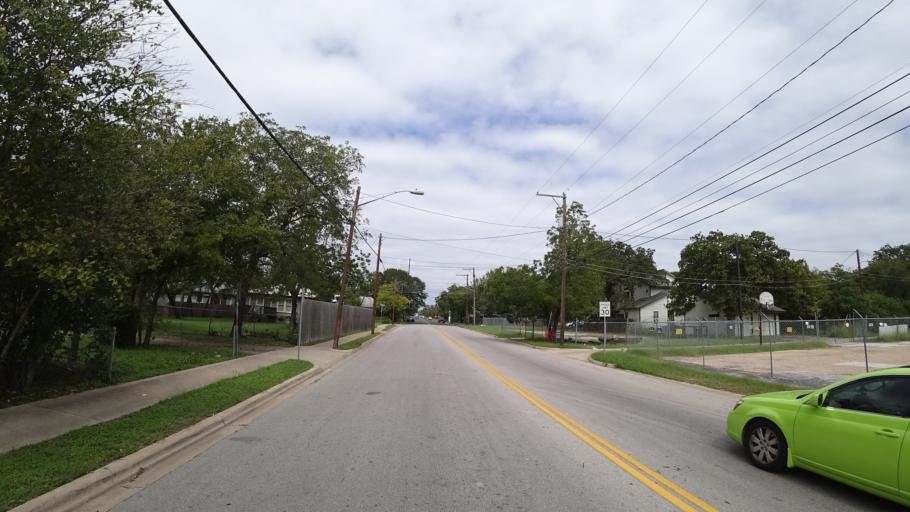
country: US
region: Texas
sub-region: Travis County
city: Austin
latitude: 30.2735
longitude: -97.7239
